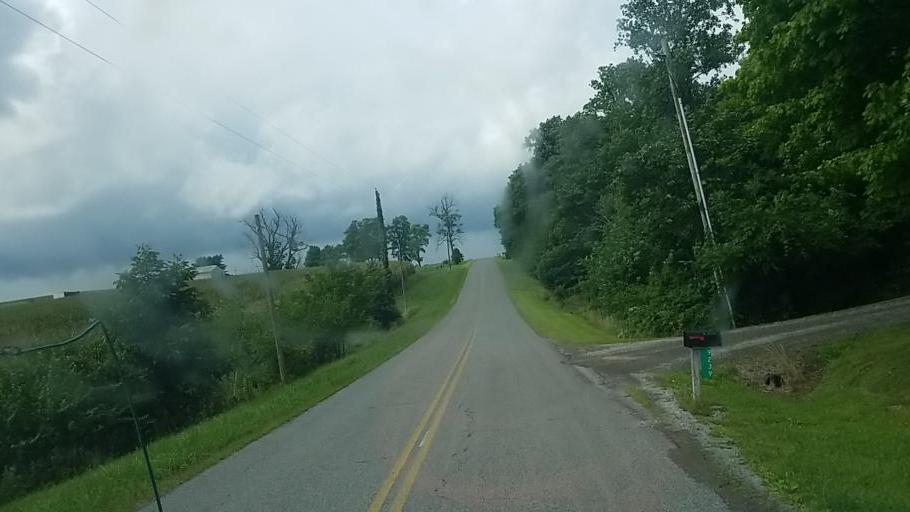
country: US
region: Ohio
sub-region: Champaign County
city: North Lewisburg
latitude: 40.2472
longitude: -83.6495
